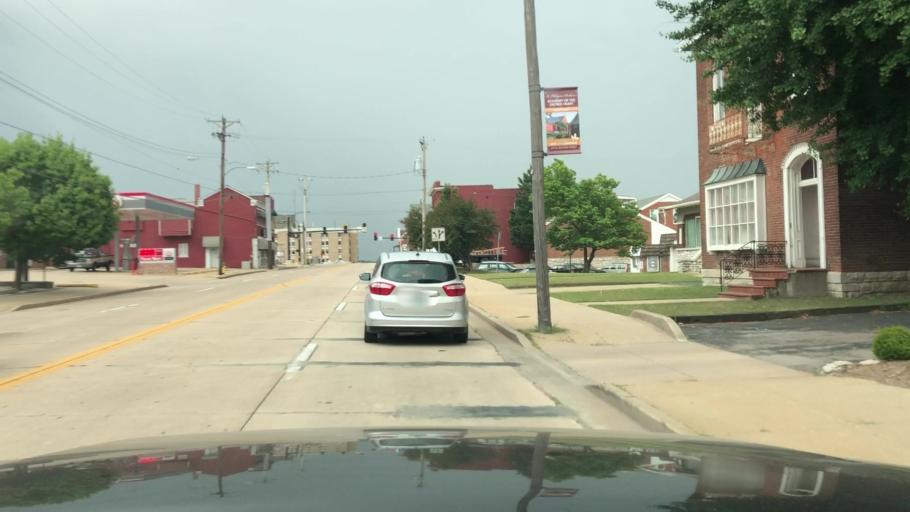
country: US
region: Missouri
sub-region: Saint Charles County
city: Saint Charles
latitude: 38.7816
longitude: -90.4887
